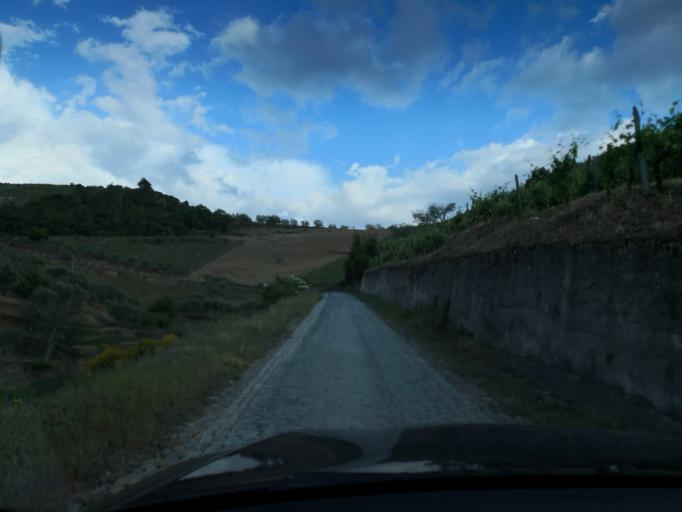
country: PT
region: Vila Real
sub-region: Vila Real
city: Vila Real
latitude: 41.2200
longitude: -7.7134
